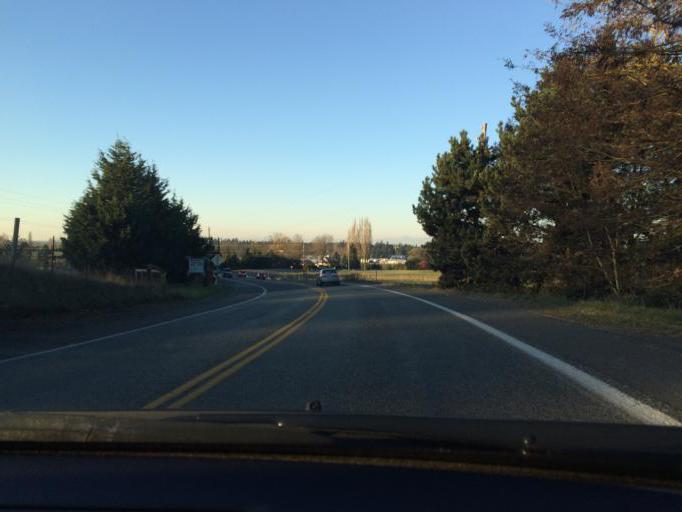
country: US
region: Washington
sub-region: Whatcom County
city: Lynden
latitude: 48.8536
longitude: -122.4410
